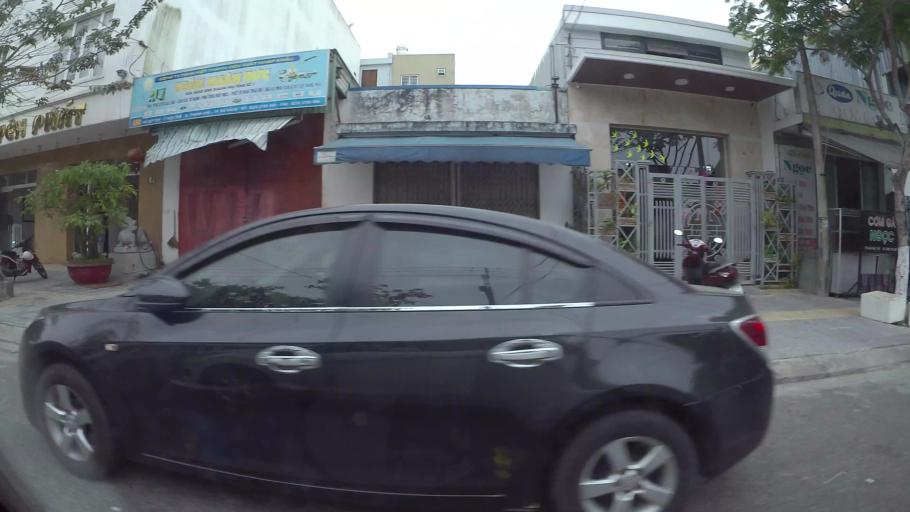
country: VN
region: Da Nang
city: Thanh Khe
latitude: 16.0627
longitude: 108.1918
